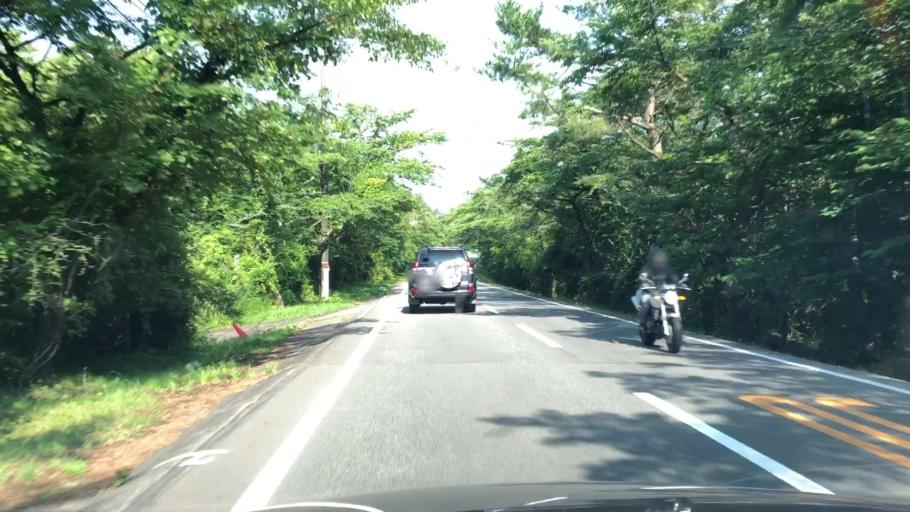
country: JP
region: Shizuoka
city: Gotemba
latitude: 35.3277
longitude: 138.8504
